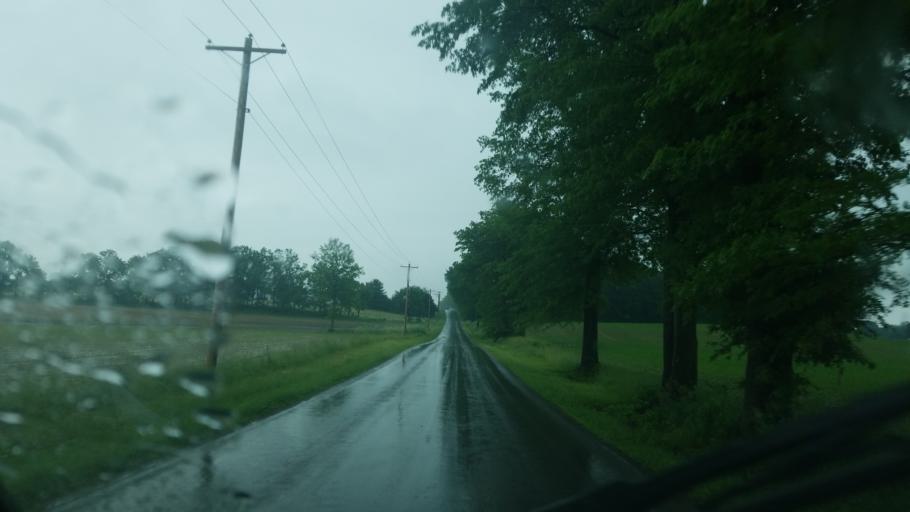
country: US
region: Ohio
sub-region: Huron County
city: Plymouth
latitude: 40.9737
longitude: -82.6202
